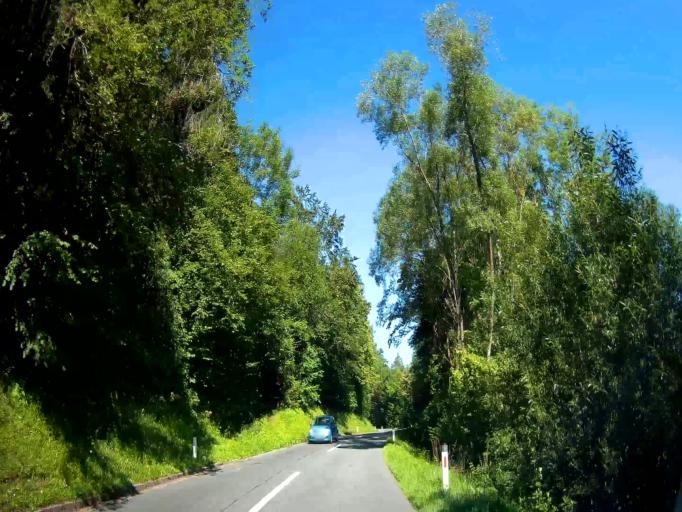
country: AT
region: Carinthia
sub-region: Politischer Bezirk Klagenfurt Land
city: Grafenstein
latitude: 46.6008
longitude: 14.4301
